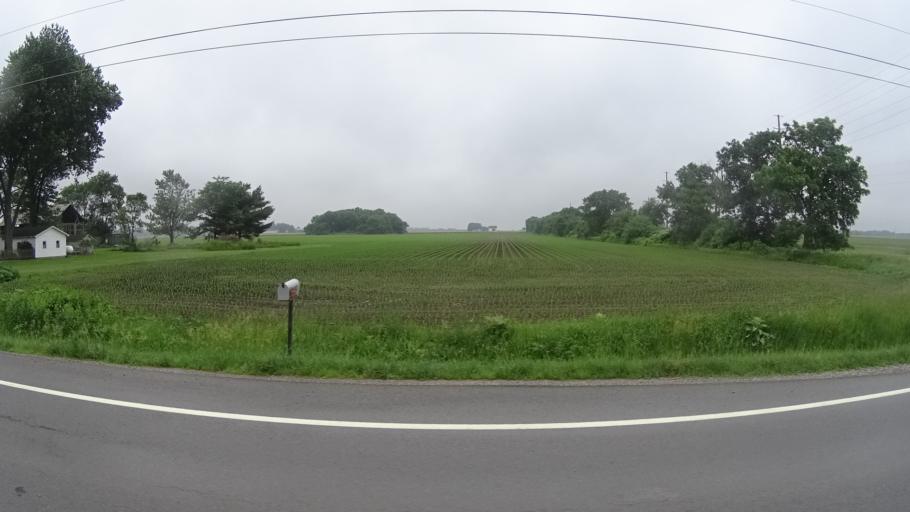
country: US
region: Ohio
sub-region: Huron County
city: Bellevue
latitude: 41.3317
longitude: -82.8300
